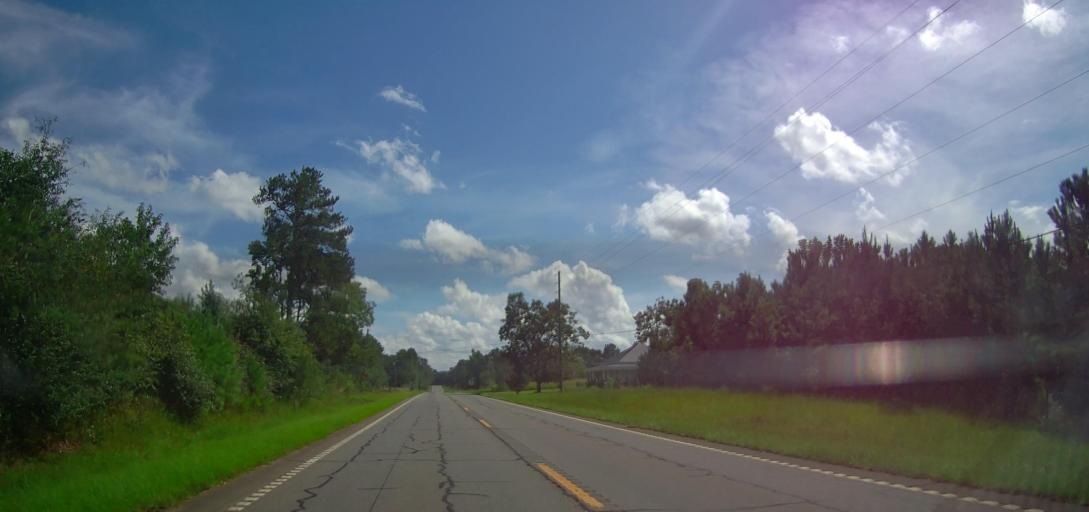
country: US
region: Georgia
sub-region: Talbot County
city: Sardis
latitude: 32.7644
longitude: -84.5583
